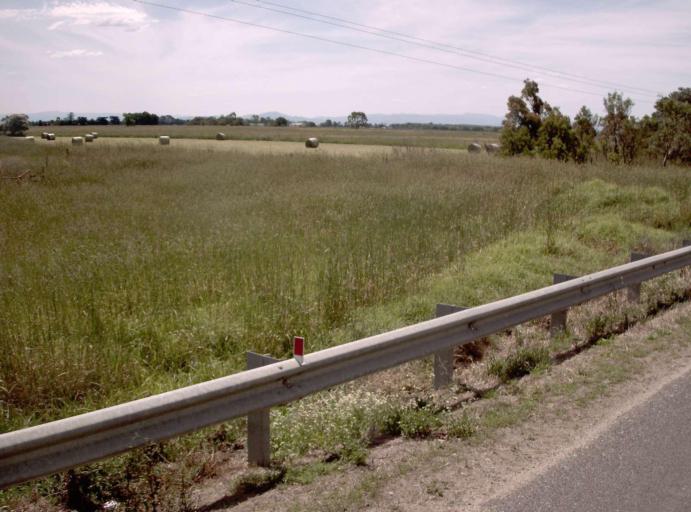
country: AU
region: Victoria
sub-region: Wellington
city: Sale
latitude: -38.0727
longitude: 147.0730
